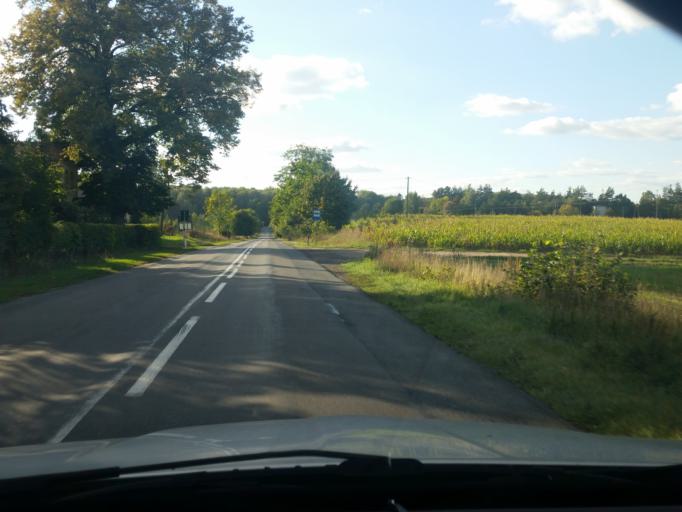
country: PL
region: Pomeranian Voivodeship
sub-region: Powiat chojnicki
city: Chojnice
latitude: 53.7202
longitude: 17.5012
